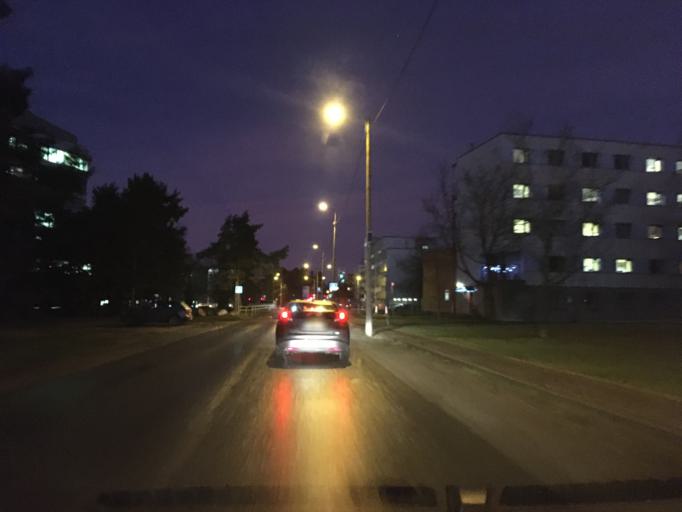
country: EE
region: Harju
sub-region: Saue vald
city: Laagri
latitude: 59.3959
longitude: 24.6626
